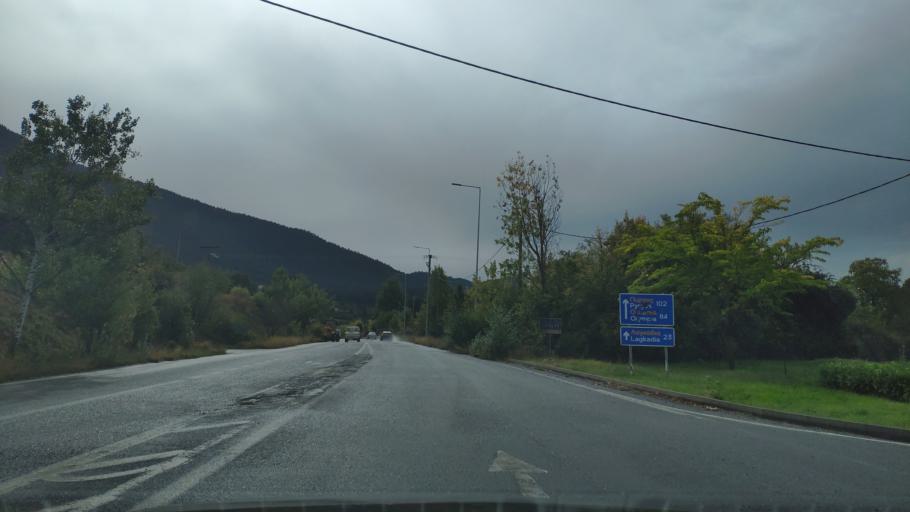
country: GR
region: Peloponnese
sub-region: Nomos Arkadias
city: Langadhia
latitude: 37.6741
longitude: 22.1925
